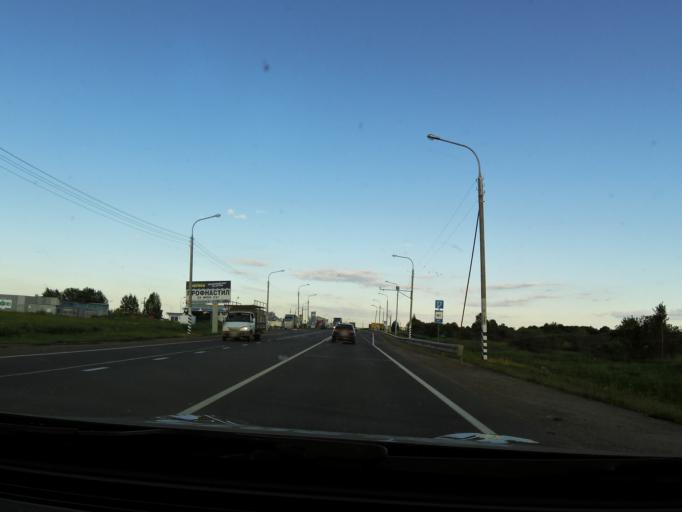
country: RU
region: Vologda
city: Vologda
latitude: 59.1731
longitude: 39.9028
